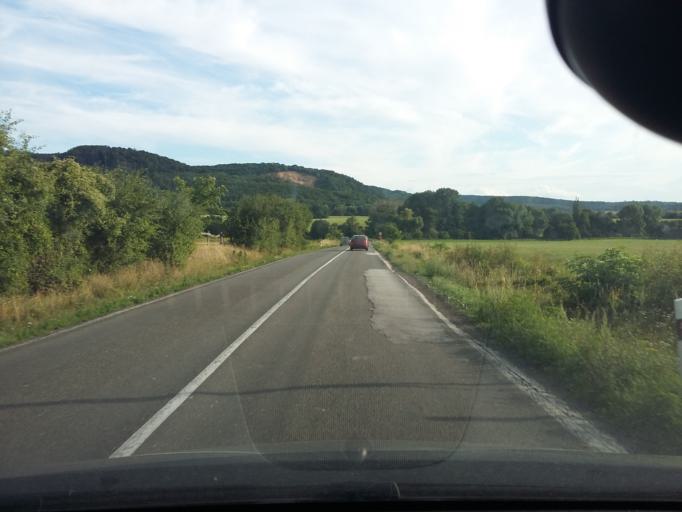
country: SK
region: Bratislavsky
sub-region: Okres Malacky
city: Malacky
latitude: 48.3873
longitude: 17.1549
